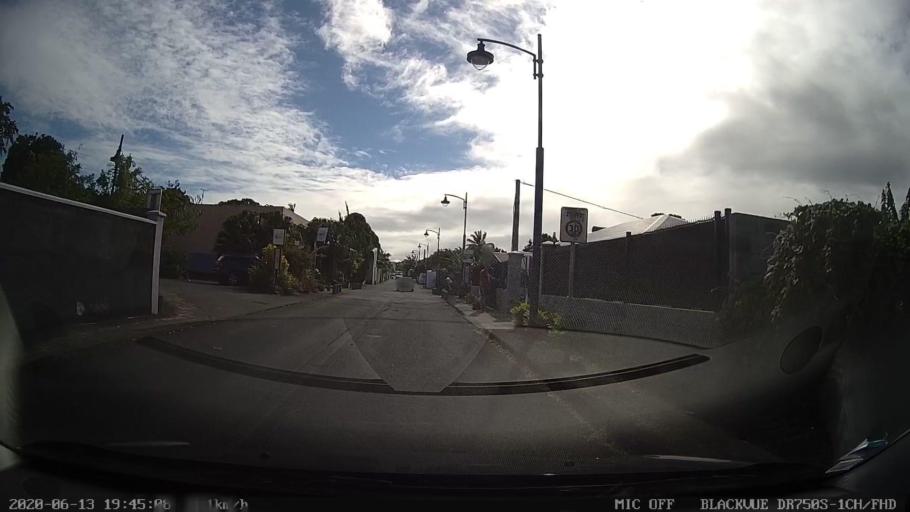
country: RE
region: Reunion
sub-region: Reunion
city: Bras-Panon
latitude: -20.9984
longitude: 55.6768
